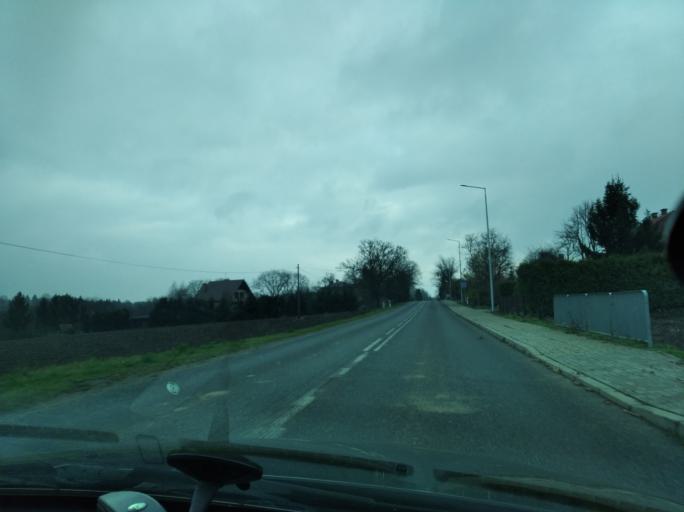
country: PL
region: Subcarpathian Voivodeship
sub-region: Powiat przeworski
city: Sietesz
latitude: 50.0041
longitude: 22.3482
